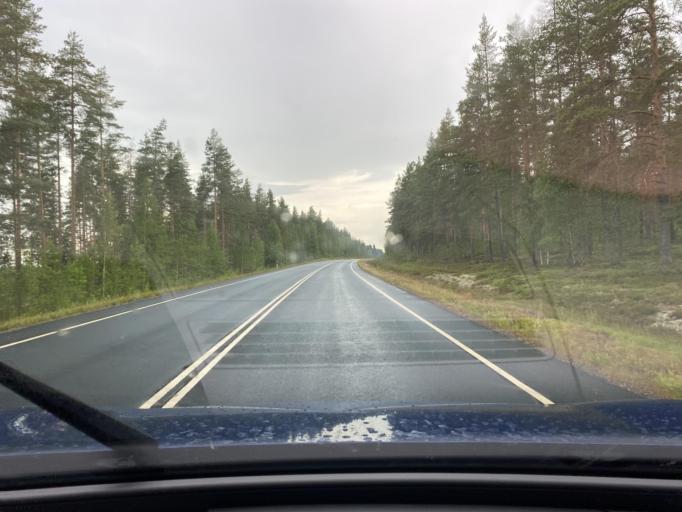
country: FI
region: Central Ostrobothnia
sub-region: Kaustinen
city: Veteli
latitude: 63.4118
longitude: 23.9562
